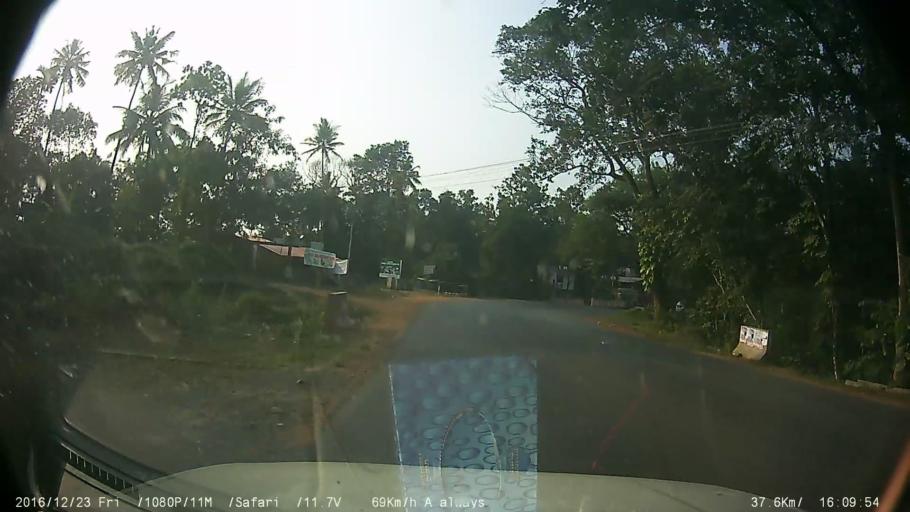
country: IN
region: Kerala
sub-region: Kottayam
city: Palackattumala
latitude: 9.7026
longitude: 76.5560
